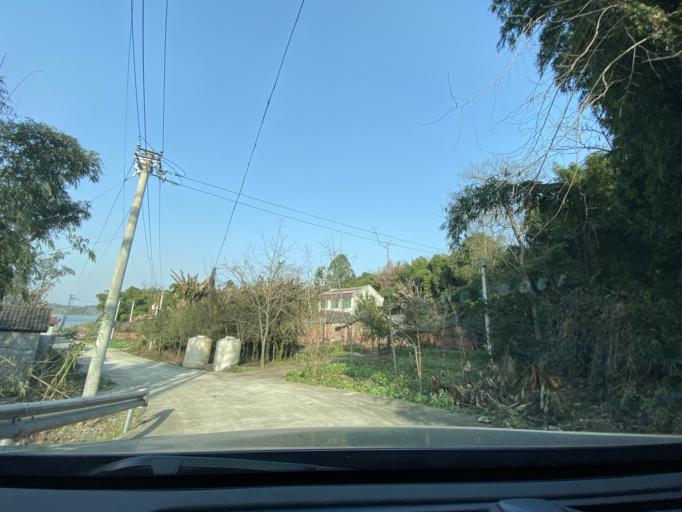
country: CN
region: Sichuan
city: Wenlin
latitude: 30.2527
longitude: 104.2545
